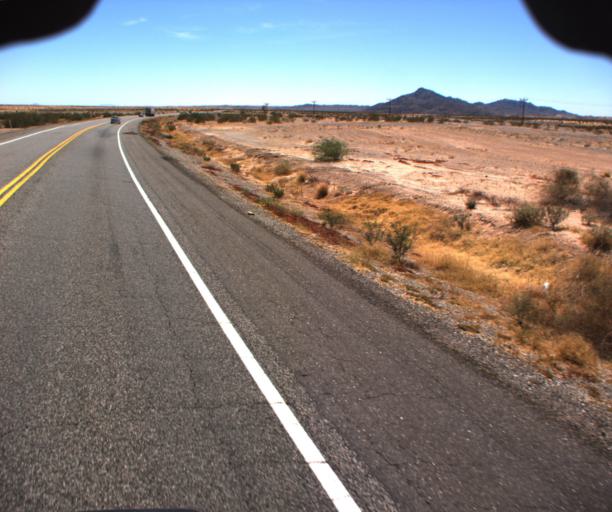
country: US
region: Arizona
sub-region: La Paz County
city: Parker
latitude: 34.0667
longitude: -114.2580
